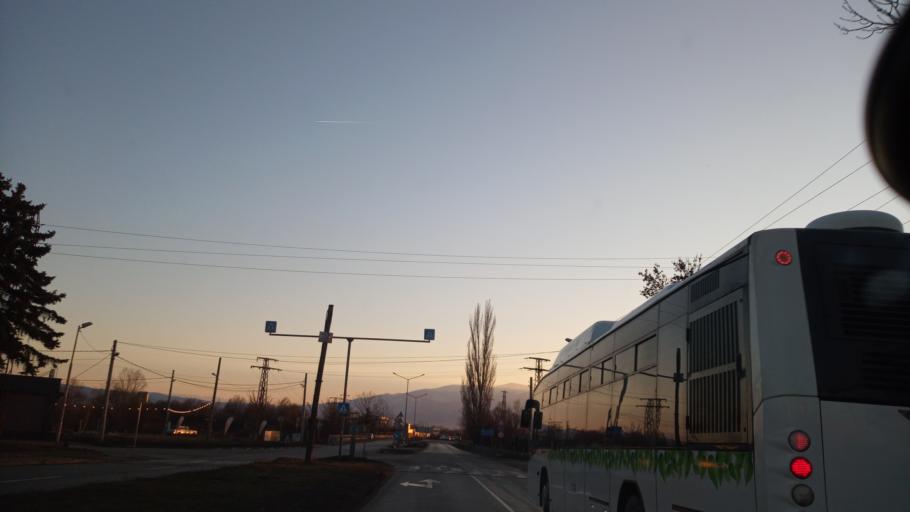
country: BG
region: Sofia-Capital
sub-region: Stolichna Obshtina
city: Bukhovo
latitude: 42.7332
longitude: 23.4657
